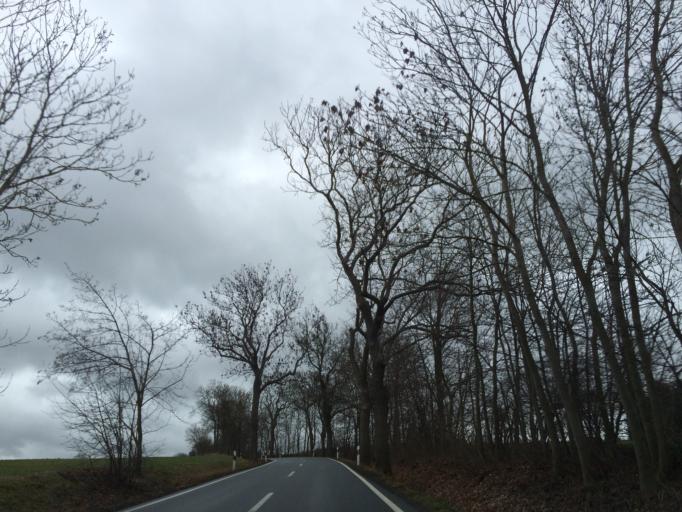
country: DE
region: Thuringia
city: Bodelwitz
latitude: 50.6698
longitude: 11.6160
